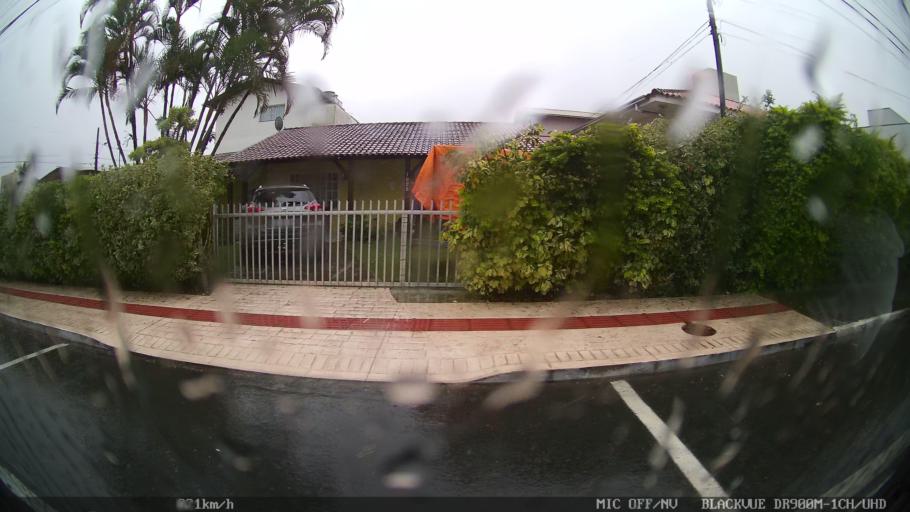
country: BR
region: Santa Catarina
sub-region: Balneario Camboriu
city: Balneario Camboriu
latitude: -27.0133
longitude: -48.6327
